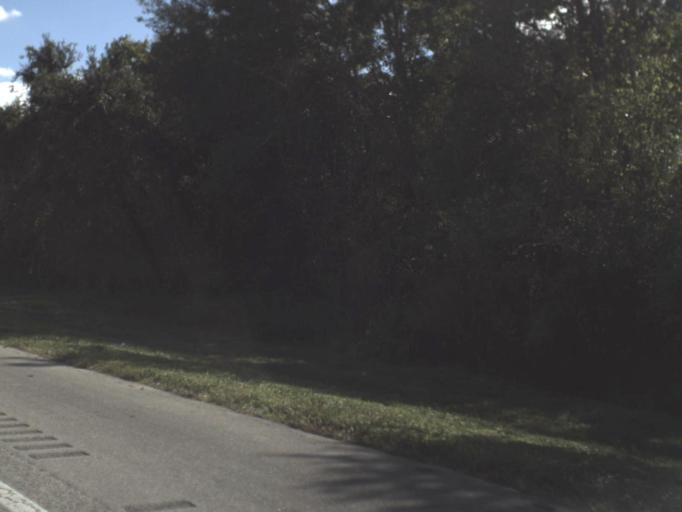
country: US
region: Florida
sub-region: Indian River County
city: Fellsmere
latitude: 27.5817
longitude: -80.8081
